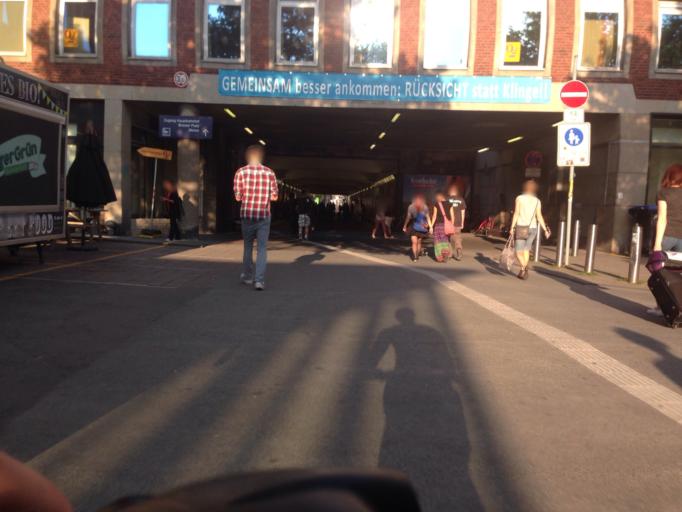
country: DE
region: North Rhine-Westphalia
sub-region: Regierungsbezirk Munster
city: Muenster
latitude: 51.9561
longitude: 7.6344
